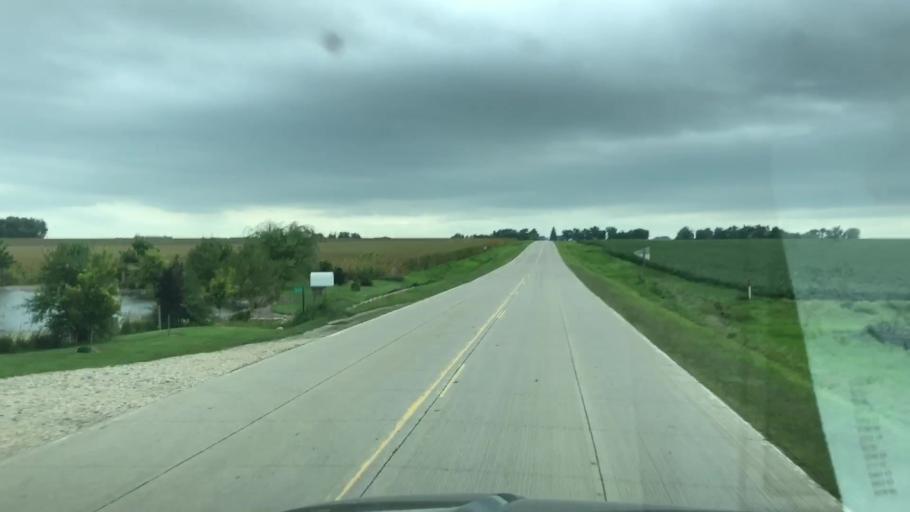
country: US
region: Iowa
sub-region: Sioux County
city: Alton
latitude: 43.1198
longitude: -95.9789
